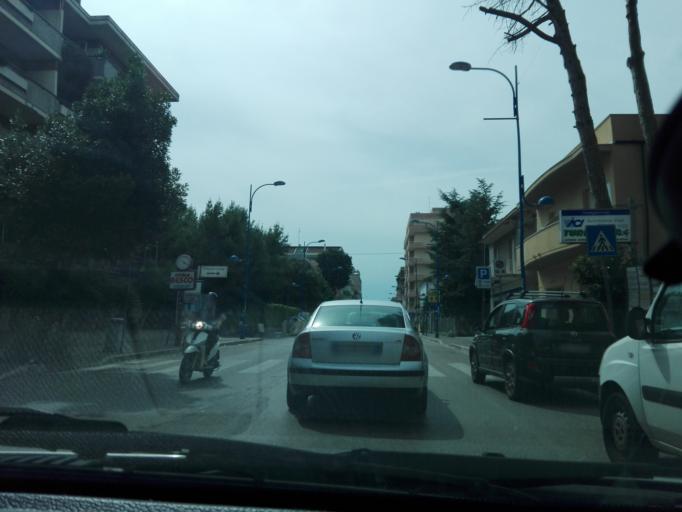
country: IT
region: Abruzzo
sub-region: Provincia di Pescara
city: Montesilvano Marina
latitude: 42.5143
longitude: 14.1524
